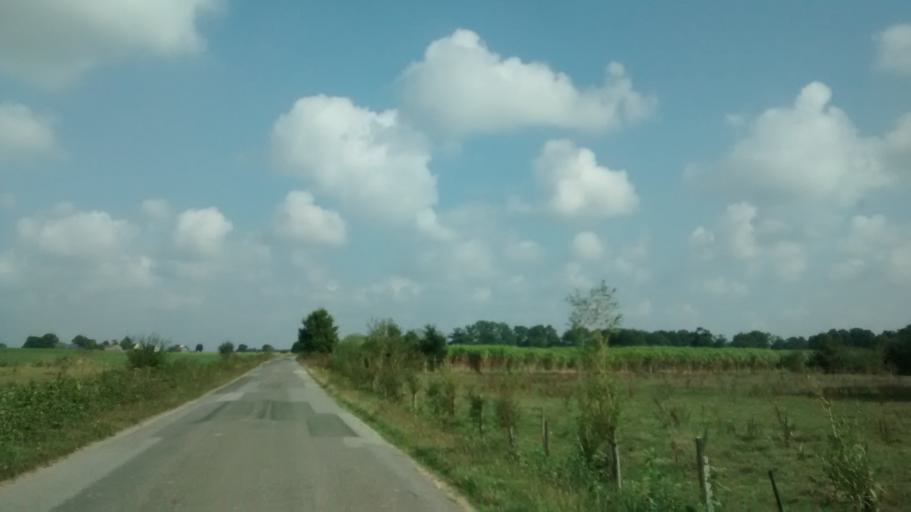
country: FR
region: Brittany
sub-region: Departement d'Ille-et-Vilaine
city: Erbree
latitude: 48.1284
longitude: -1.1024
